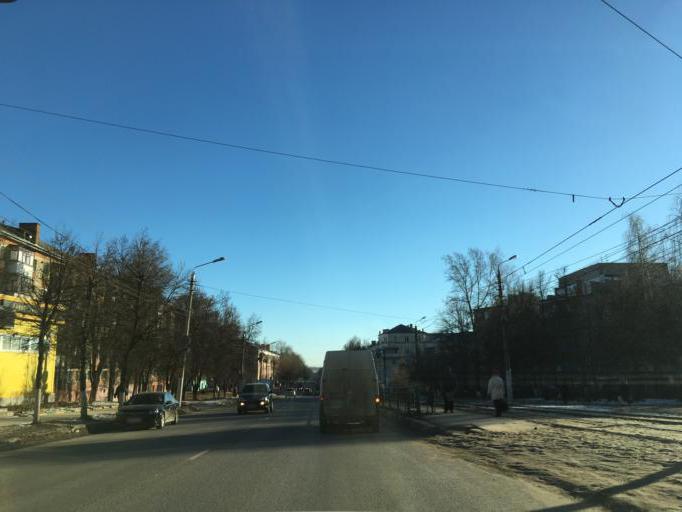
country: RU
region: Tula
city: Tula
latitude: 54.1879
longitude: 37.6931
